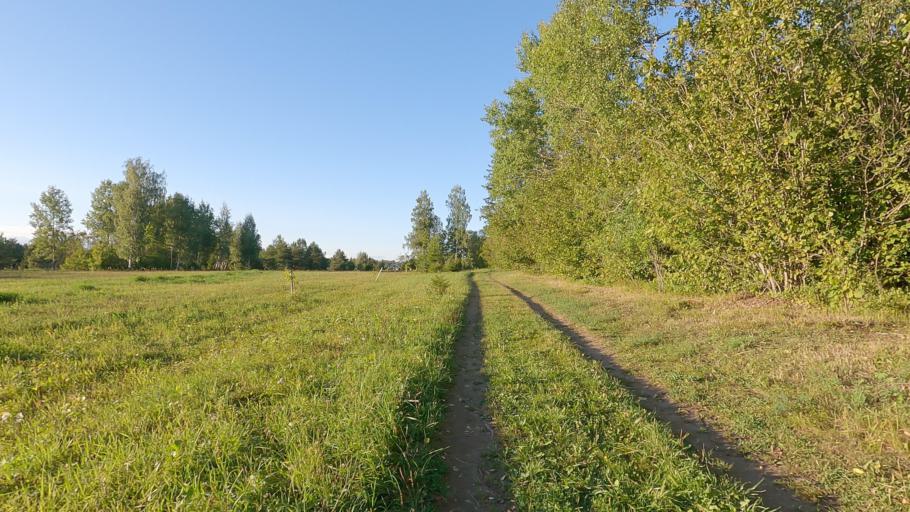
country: EE
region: Raplamaa
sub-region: Rapla vald
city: Rapla
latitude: 59.0000
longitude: 24.7812
